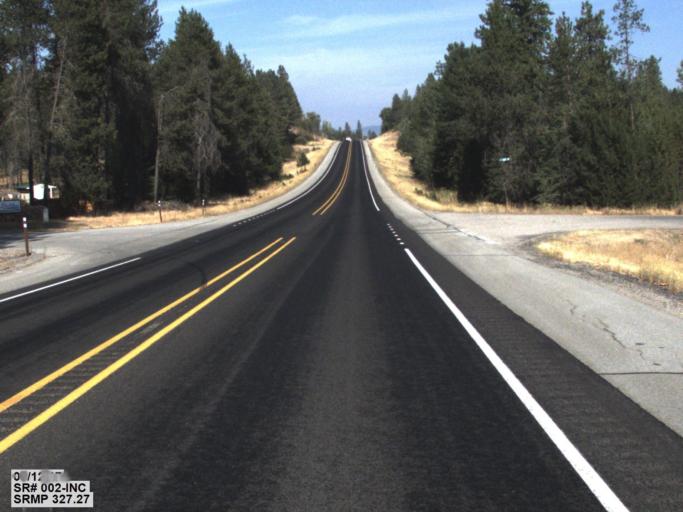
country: US
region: Washington
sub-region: Pend Oreille County
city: Newport
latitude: 48.1359
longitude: -117.1684
